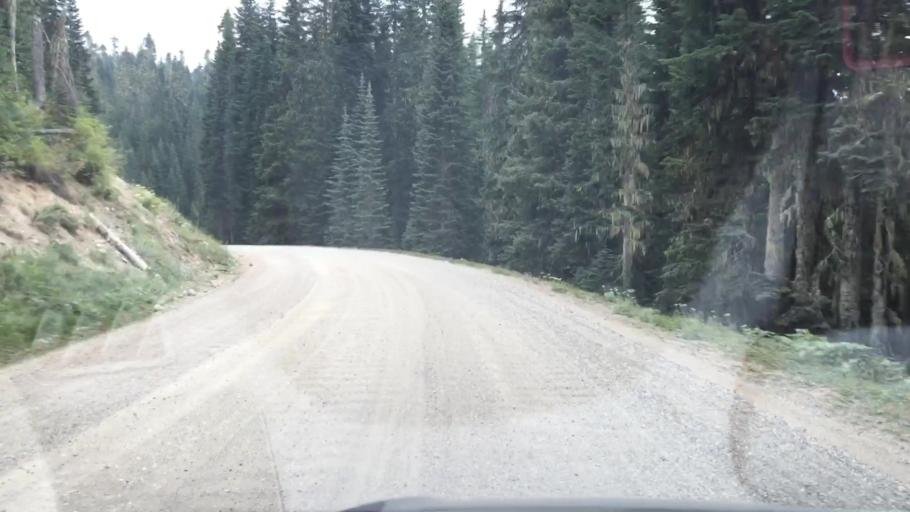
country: US
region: Washington
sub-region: Klickitat County
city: White Salmon
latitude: 46.2730
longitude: -121.6019
